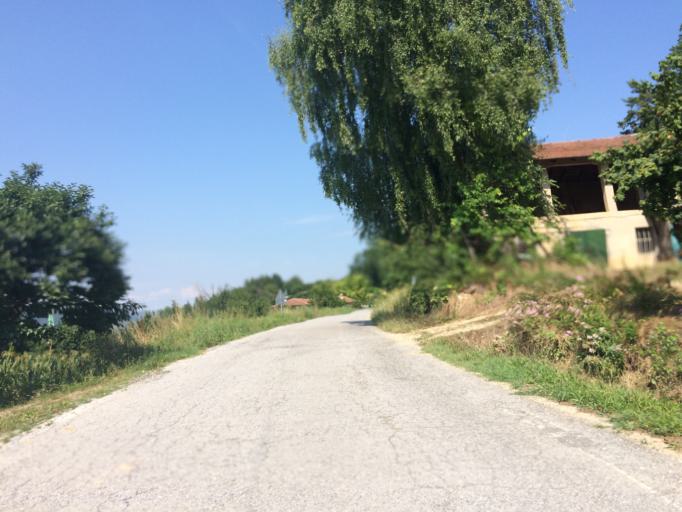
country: IT
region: Piedmont
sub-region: Provincia di Cuneo
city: Cravanzana
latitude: 44.5833
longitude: 8.1287
